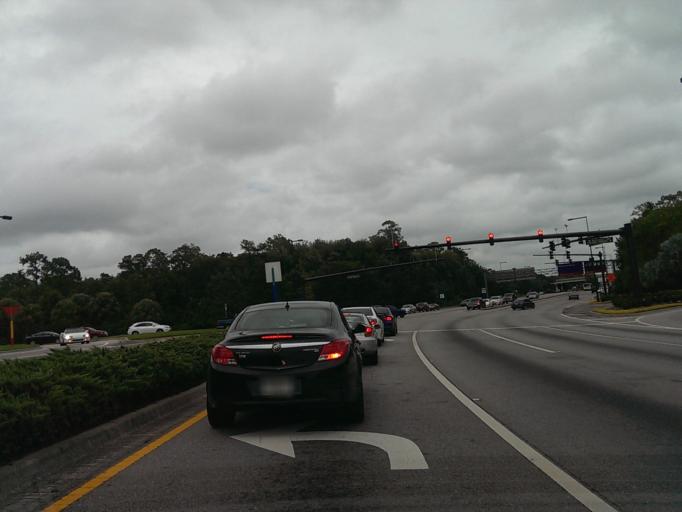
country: US
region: Florida
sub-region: Osceola County
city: Celebration
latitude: 28.3694
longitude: -81.5416
